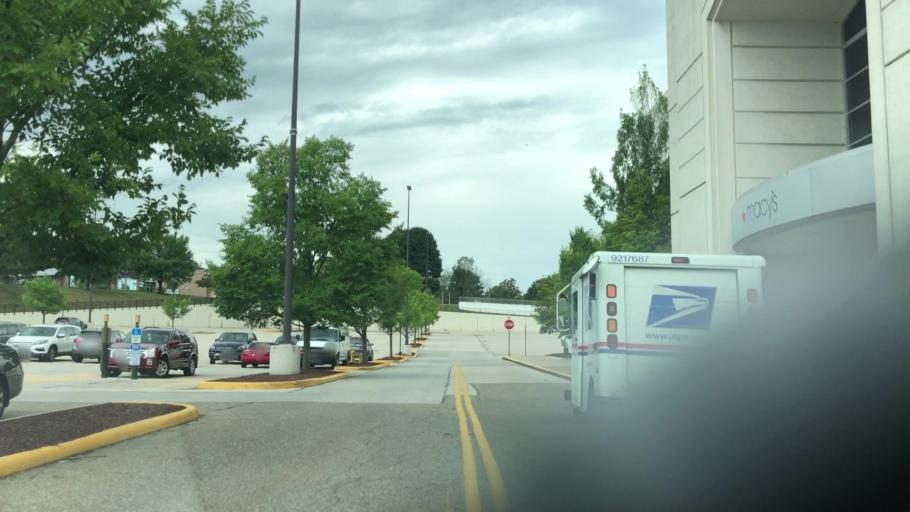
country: US
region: Ohio
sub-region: Summit County
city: Fairlawn
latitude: 41.1340
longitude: -81.6195
